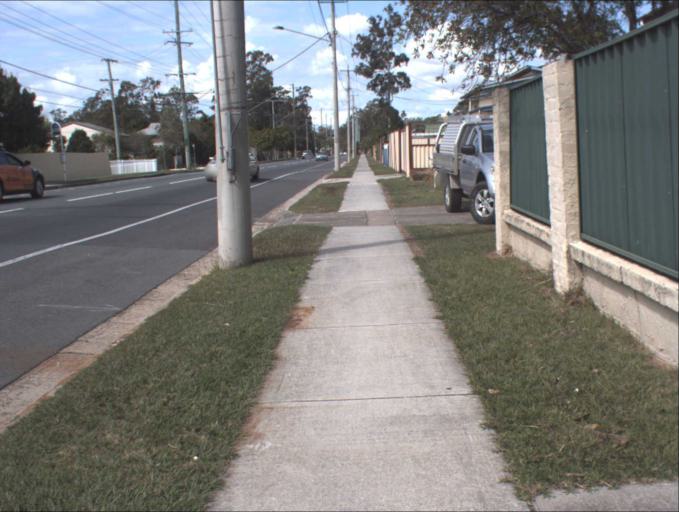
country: AU
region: Queensland
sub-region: Logan
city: Waterford West
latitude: -27.6822
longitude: 153.1070
